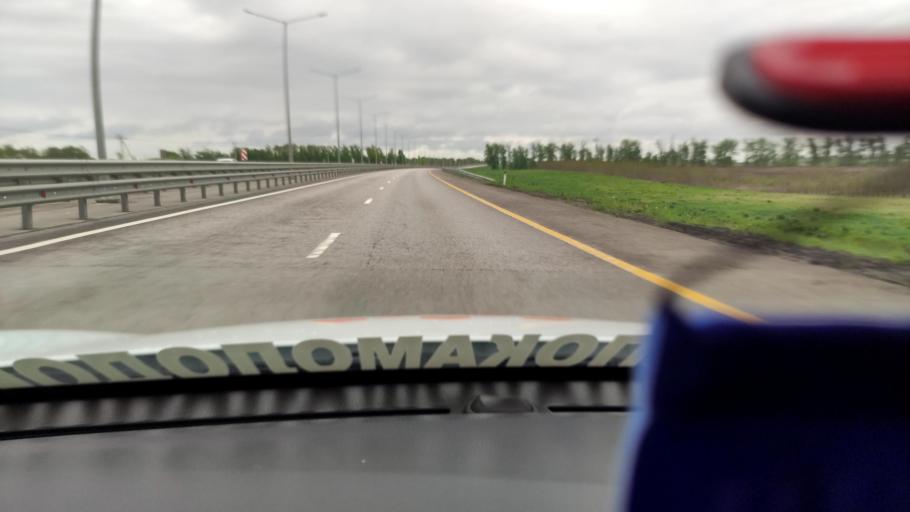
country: RU
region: Voronezj
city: Podkletnoye
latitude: 51.5824
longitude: 39.4582
